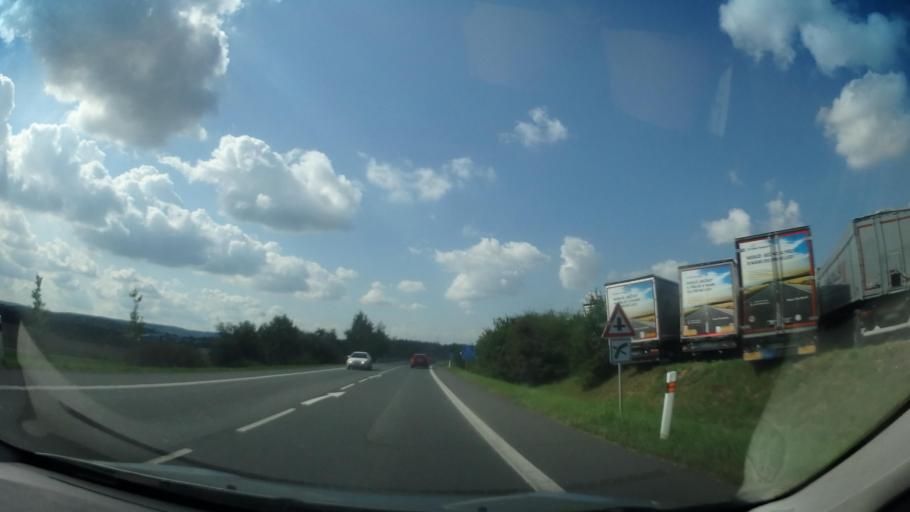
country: CZ
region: Central Bohemia
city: Kostelec nad Cernymi Lesy
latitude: 49.9850
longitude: 14.8508
